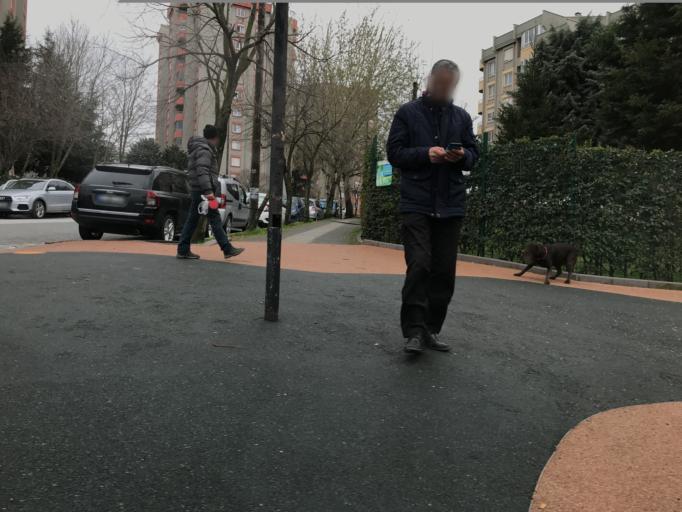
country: TR
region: Istanbul
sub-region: Atasehir
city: Atasehir
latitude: 40.9891
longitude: 29.1353
